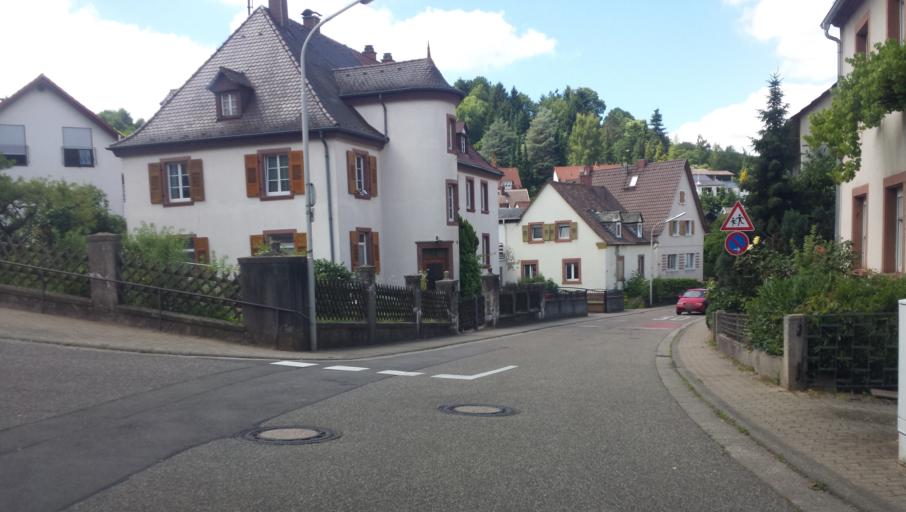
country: DE
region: Rheinland-Pfalz
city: Annweiler am Trifels
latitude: 49.2013
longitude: 7.9619
